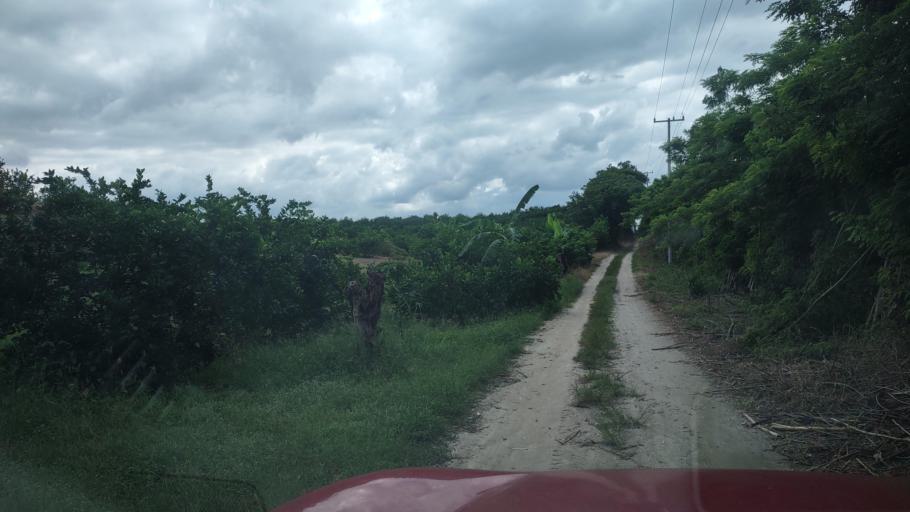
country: MX
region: Puebla
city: San Jose Acateno
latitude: 20.2123
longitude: -97.1385
